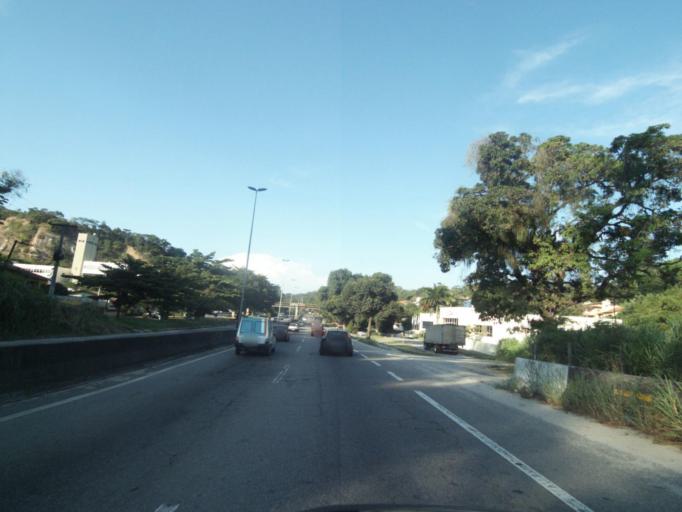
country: BR
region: Rio de Janeiro
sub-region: Niteroi
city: Niteroi
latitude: -22.8826
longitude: -43.0594
